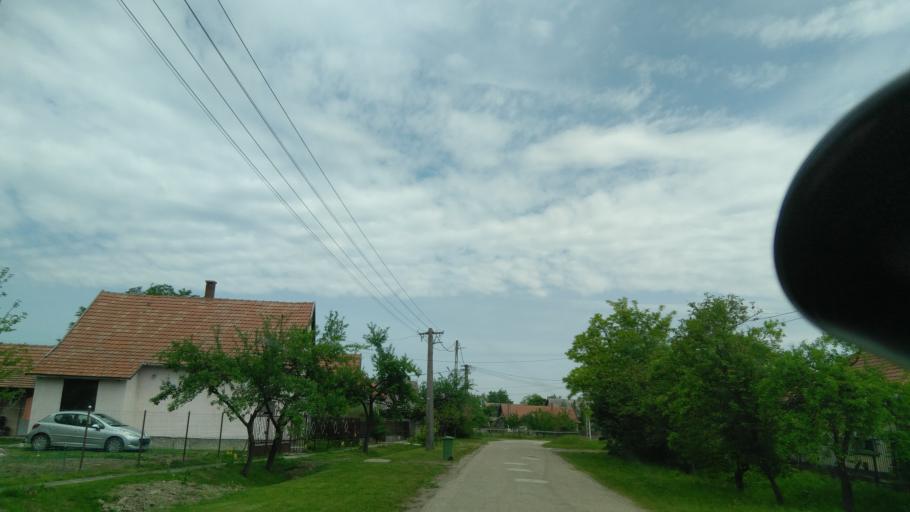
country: HU
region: Bekes
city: Fuzesgyarmat
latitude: 47.1010
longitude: 21.2147
